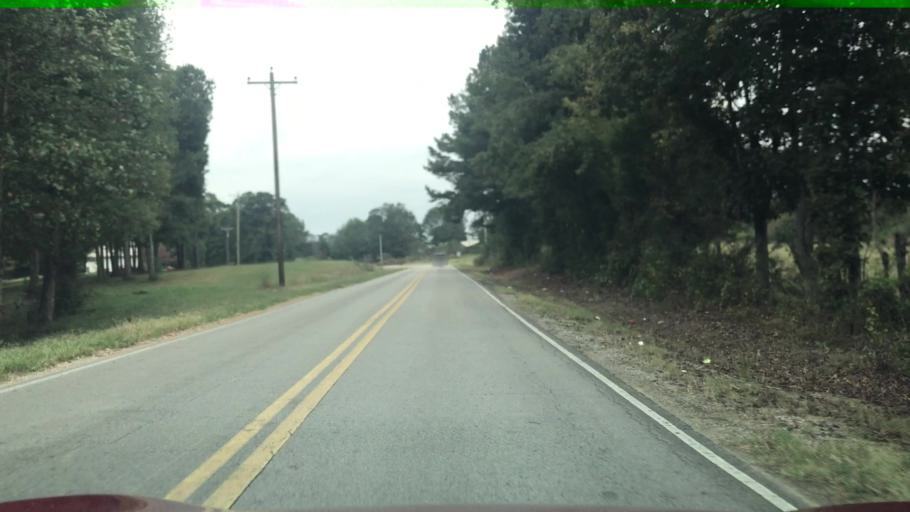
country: US
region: Alabama
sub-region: Cullman County
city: Good Hope
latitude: 34.0958
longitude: -87.0471
